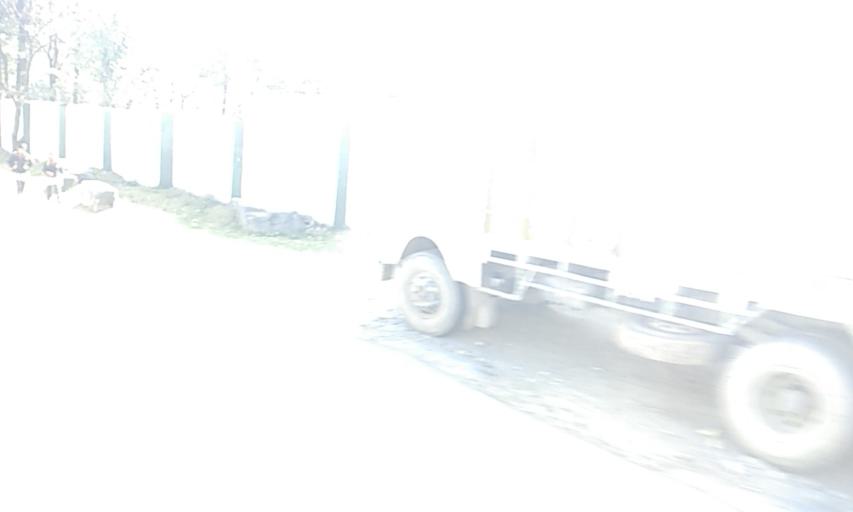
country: IN
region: Himachal Pradesh
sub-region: Kangra
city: Dharmsala
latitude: 32.1777
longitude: 76.3796
